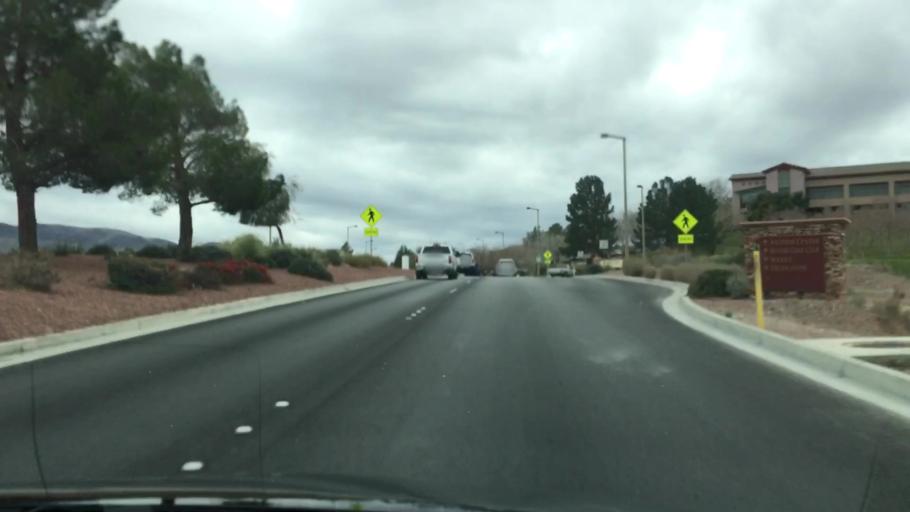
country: US
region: Nevada
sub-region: Clark County
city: Whitney
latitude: 35.9584
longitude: -115.0949
